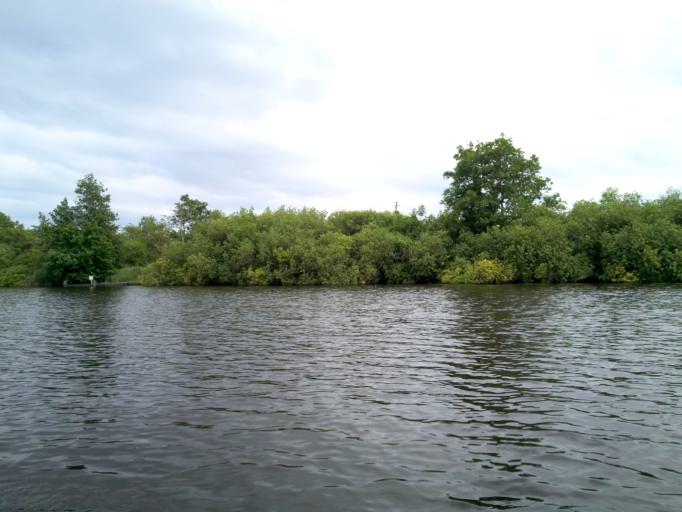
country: NL
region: Friesland
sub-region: Gemeente Boarnsterhim
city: Warten
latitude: 53.1335
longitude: 5.9080
